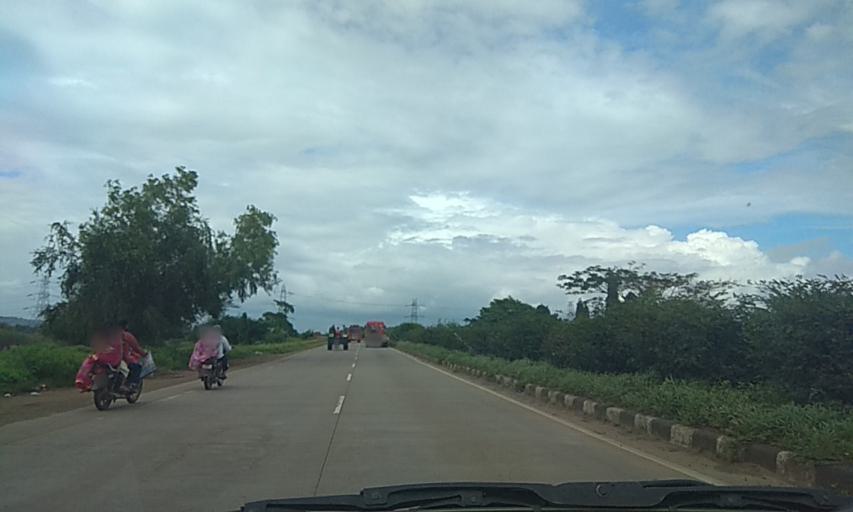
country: IN
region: Maharashtra
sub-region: Kolhapur
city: Kagal
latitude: 16.5502
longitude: 74.3181
